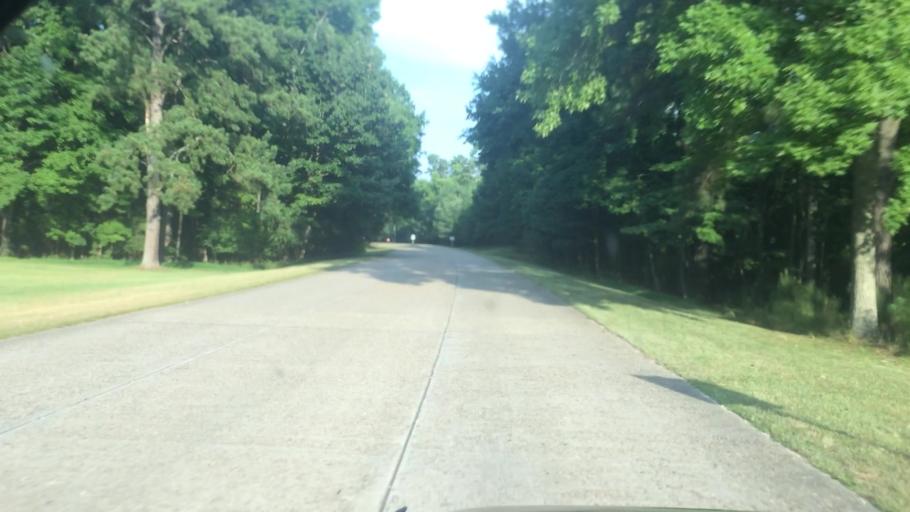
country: US
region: Virginia
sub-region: James City County
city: Williamsburg
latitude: 37.2218
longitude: -76.7736
